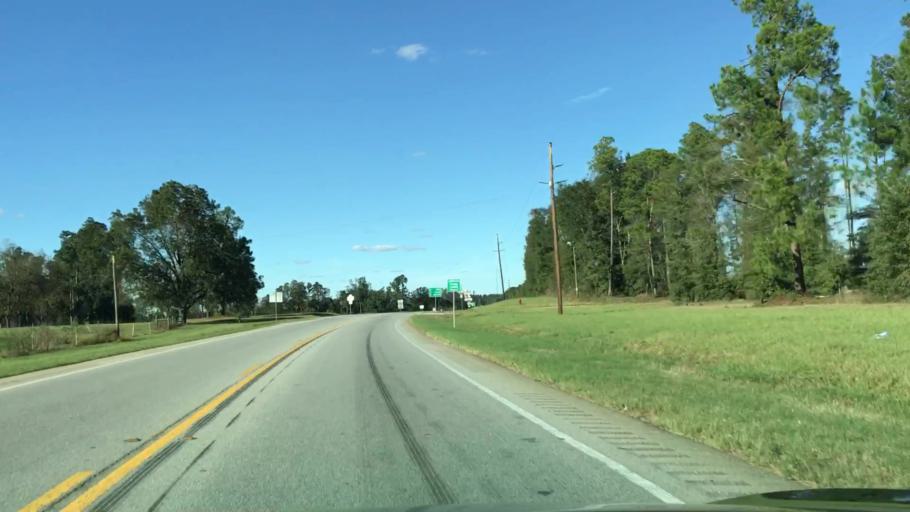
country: US
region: Georgia
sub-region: Jefferson County
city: Louisville
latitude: 33.0669
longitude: -82.4064
